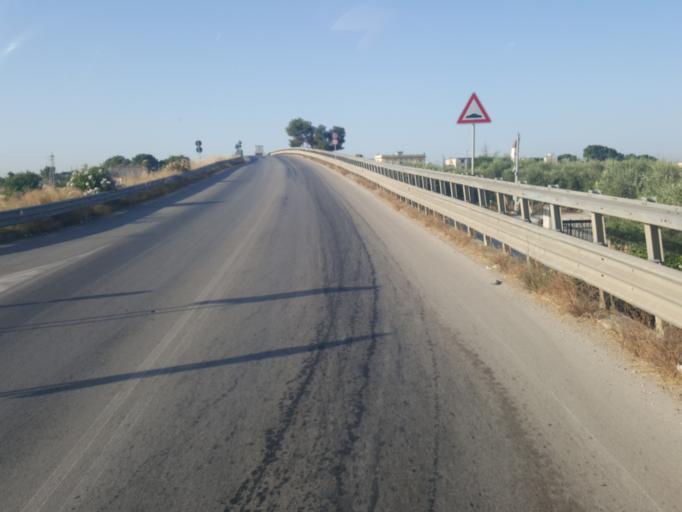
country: IT
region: Apulia
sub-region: Provincia di Foggia
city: Cerignola
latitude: 41.3186
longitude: 15.9000
